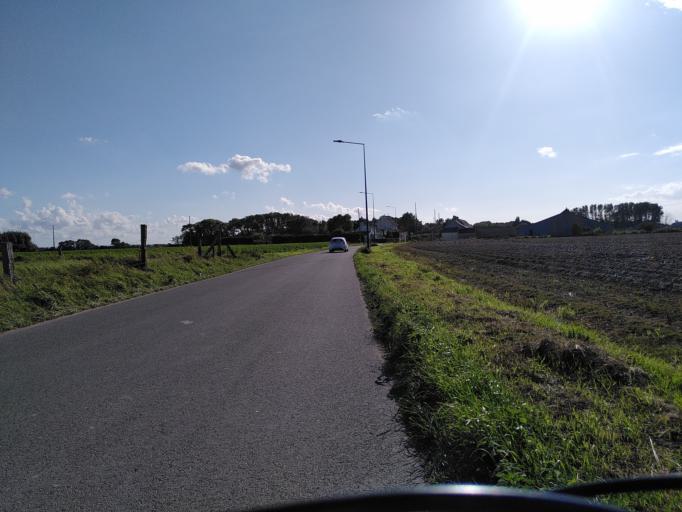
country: FR
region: Nord-Pas-de-Calais
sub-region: Departement du Pas-de-Calais
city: Marck
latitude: 50.9776
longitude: 1.9527
